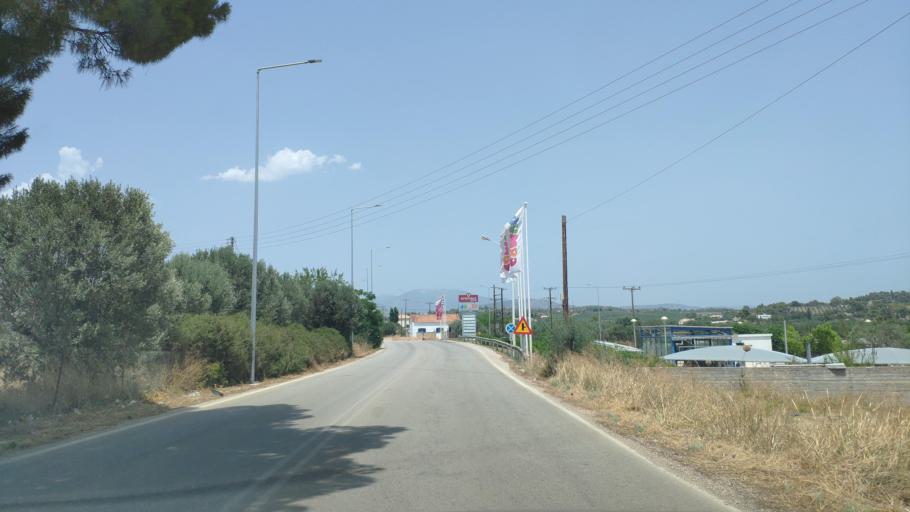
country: GR
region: Peloponnese
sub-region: Nomos Argolidos
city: Porto Cheli
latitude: 37.3416
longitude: 23.1574
